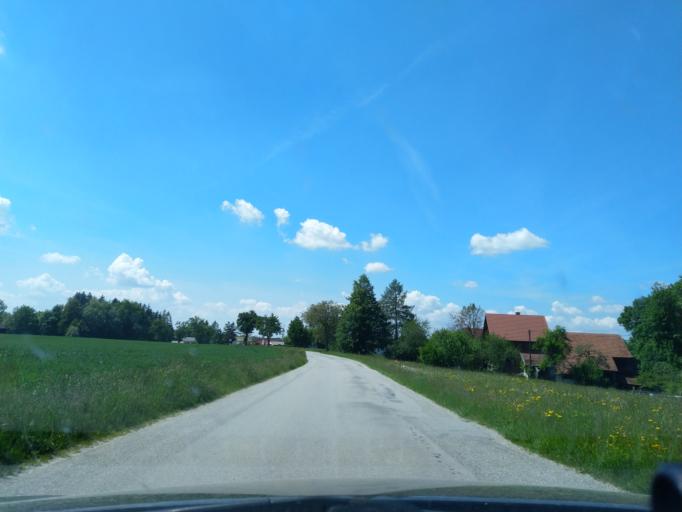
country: AT
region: Upper Austria
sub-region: Politischer Bezirk Ried im Innkreis
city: Ried im Innkreis
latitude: 48.2086
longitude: 13.5331
